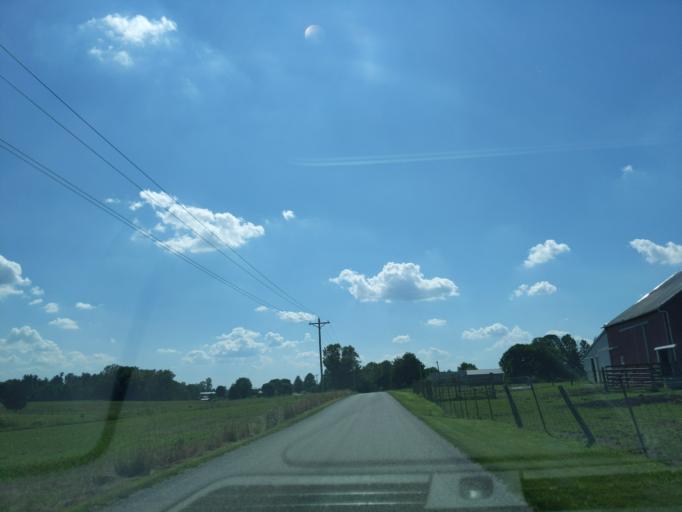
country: US
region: Indiana
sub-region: Ripley County
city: Osgood
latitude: 39.2008
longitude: -85.3735
